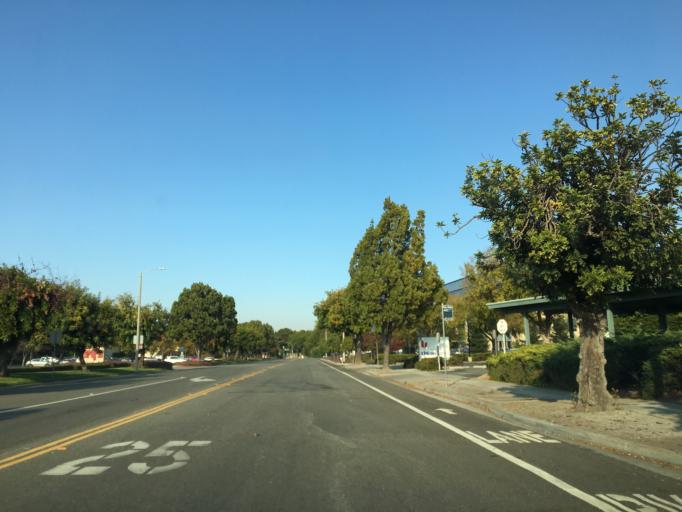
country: US
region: California
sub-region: Santa Clara County
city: Sunnyvale
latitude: 37.3808
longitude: -122.0008
